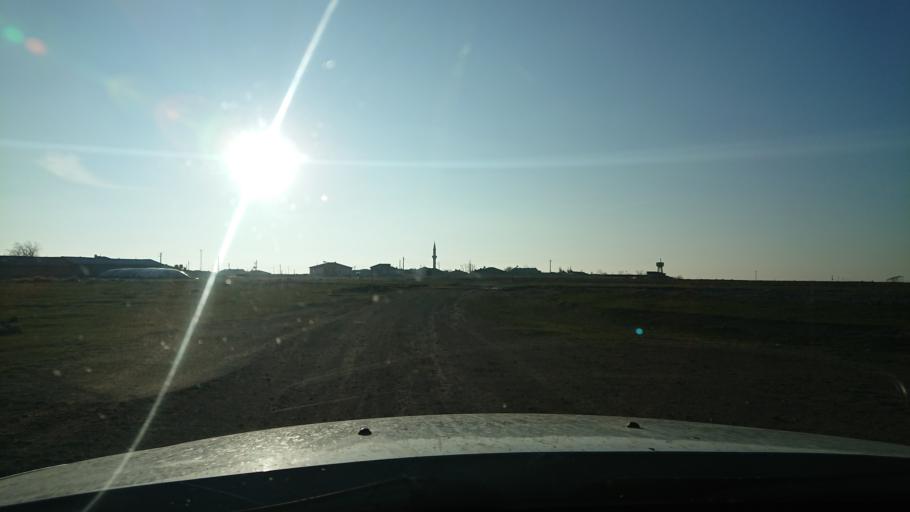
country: TR
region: Aksaray
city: Sultanhani
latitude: 38.2962
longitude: 33.5233
